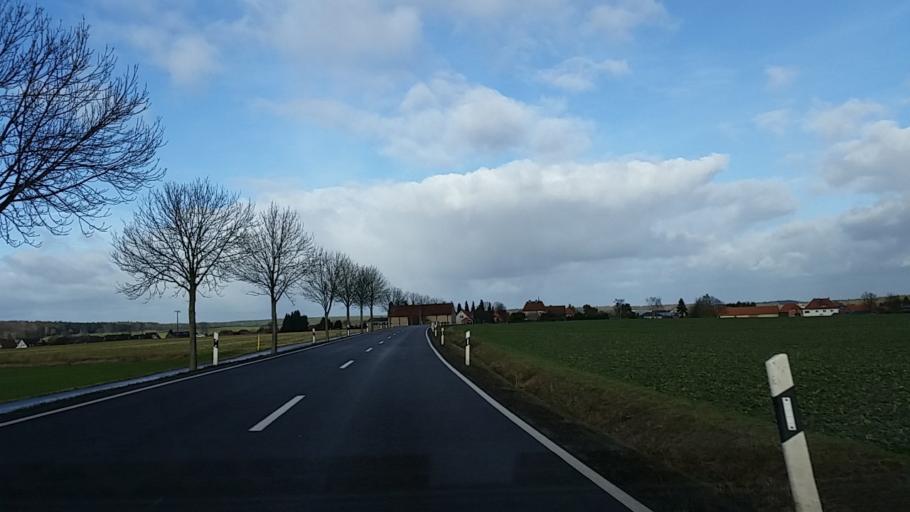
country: DE
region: Lower Saxony
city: Gross Twulpstedt
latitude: 52.3804
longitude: 10.9197
